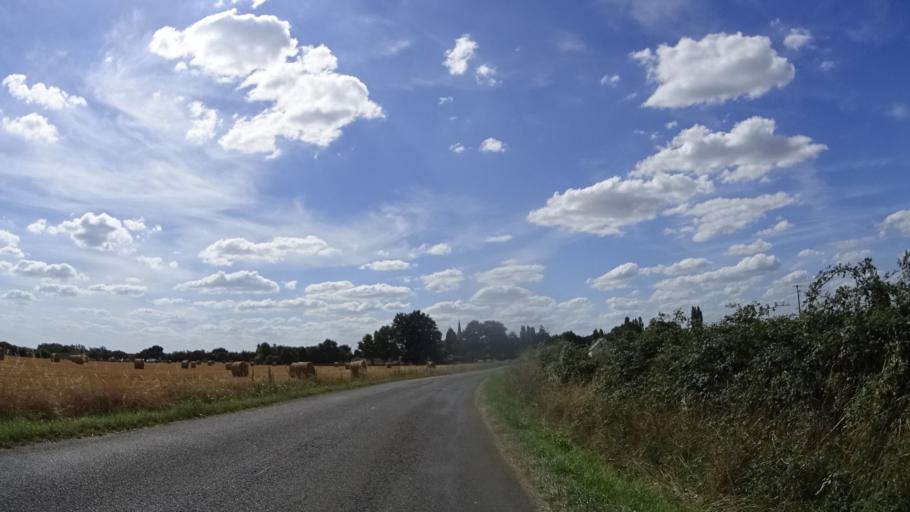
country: FR
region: Pays de la Loire
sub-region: Departement de la Loire-Atlantique
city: Saint-Mars-la-Jaille
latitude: 47.5736
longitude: -1.1986
